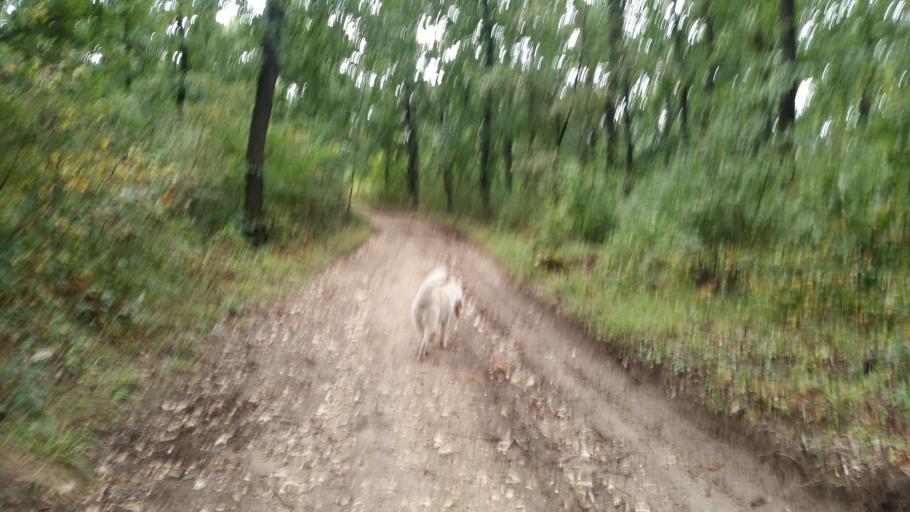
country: HU
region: Pest
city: Telki
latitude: 47.5660
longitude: 18.8220
